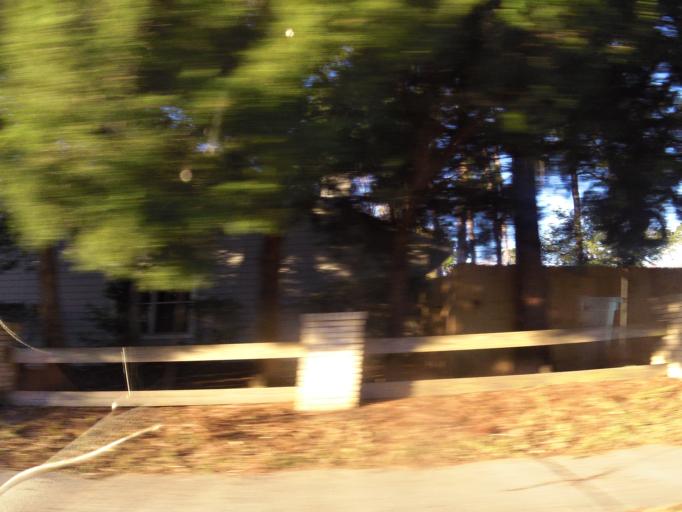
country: US
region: Florida
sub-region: Saint Johns County
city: Fruit Cove
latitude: 30.1722
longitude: -81.5963
